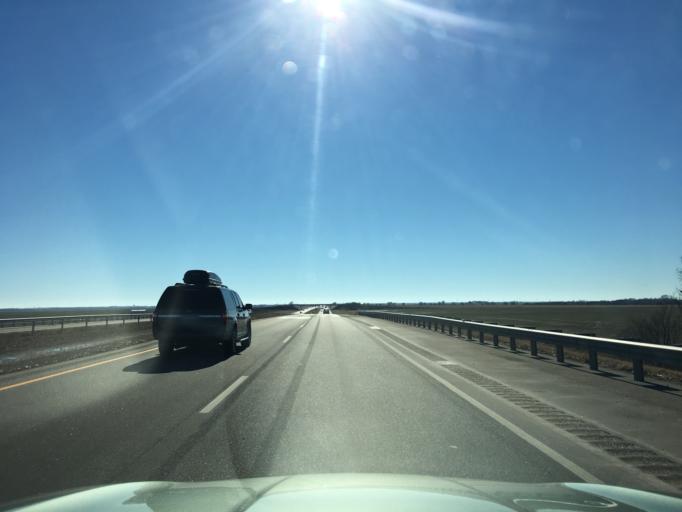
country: US
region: Oklahoma
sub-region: Kay County
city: Blackwell
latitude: 36.7742
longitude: -97.3461
